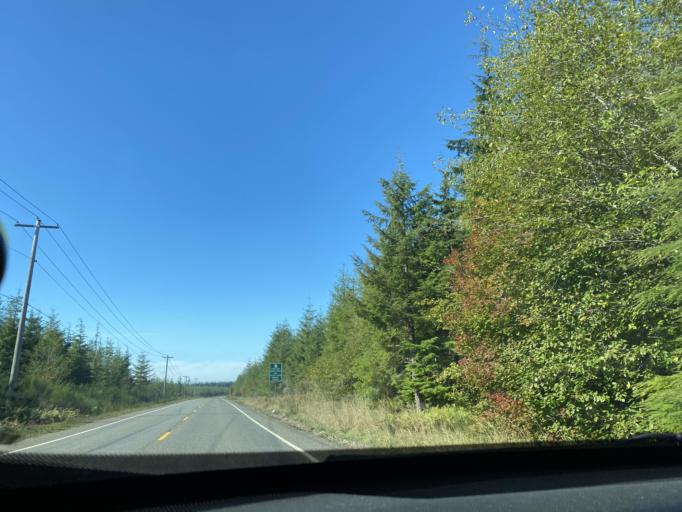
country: US
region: Washington
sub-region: Clallam County
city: Forks
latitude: 47.9655
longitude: -124.4132
